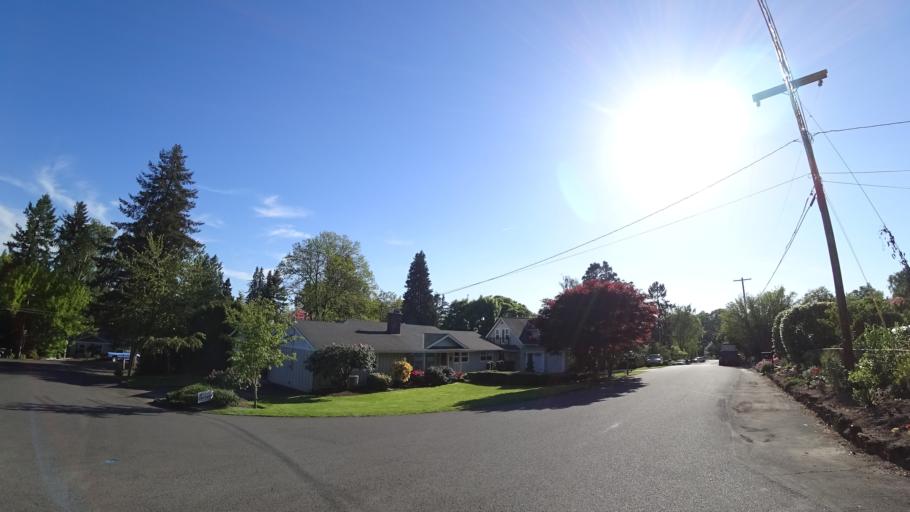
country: US
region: Oregon
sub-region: Washington County
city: West Slope
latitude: 45.4962
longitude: -122.7608
